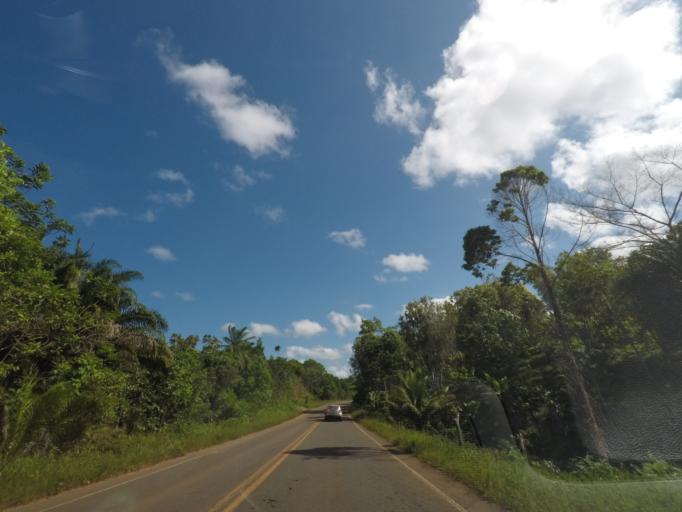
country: BR
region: Bahia
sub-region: Camamu
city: Camamu
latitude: -13.9008
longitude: -39.1339
